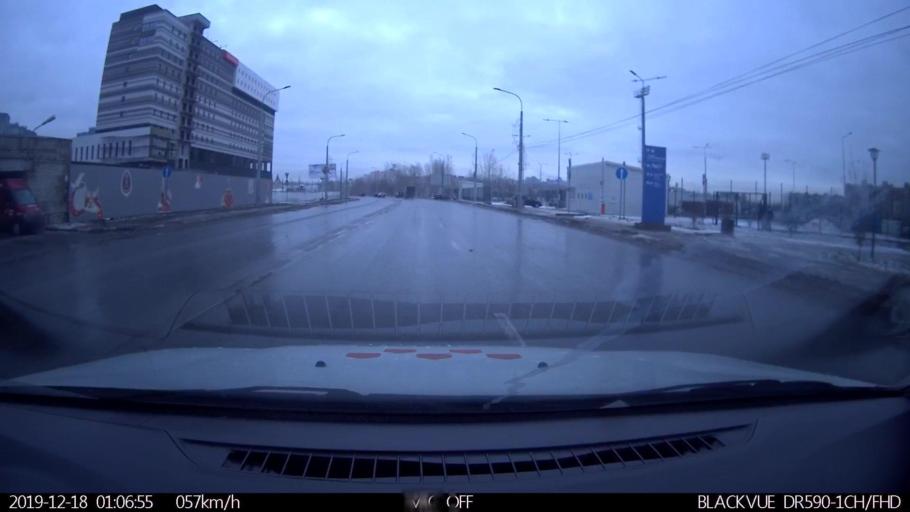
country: RU
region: Nizjnij Novgorod
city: Nizhniy Novgorod
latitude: 56.3392
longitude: 43.9454
